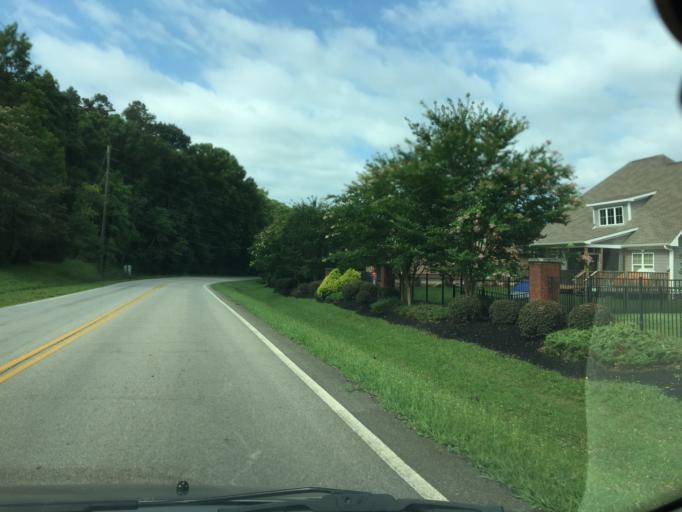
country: US
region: Tennessee
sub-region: Hamilton County
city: Apison
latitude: 35.0043
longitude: -85.0493
